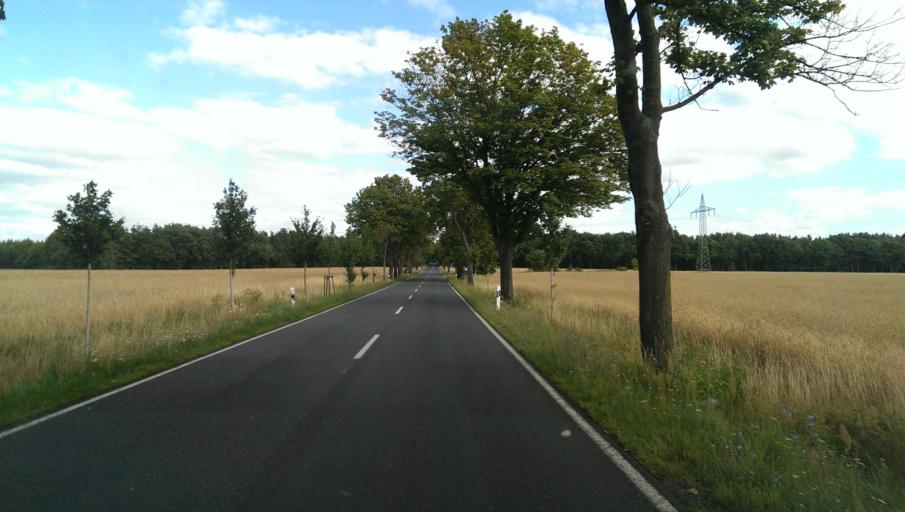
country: DE
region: Saxony-Anhalt
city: Grafenhainichen
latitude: 51.7146
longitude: 12.4742
